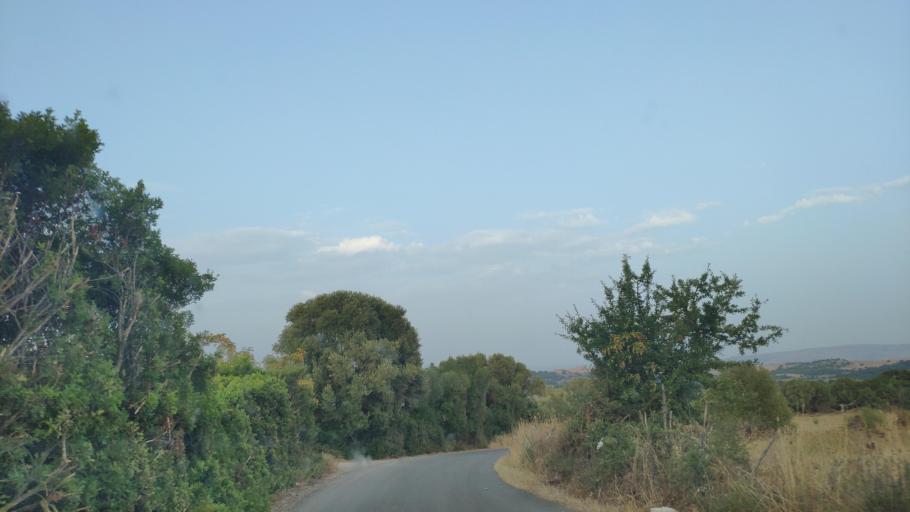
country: GR
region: West Greece
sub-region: Nomos Aitolias kai Akarnanias
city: Monastirakion
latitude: 38.9217
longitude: 20.9897
